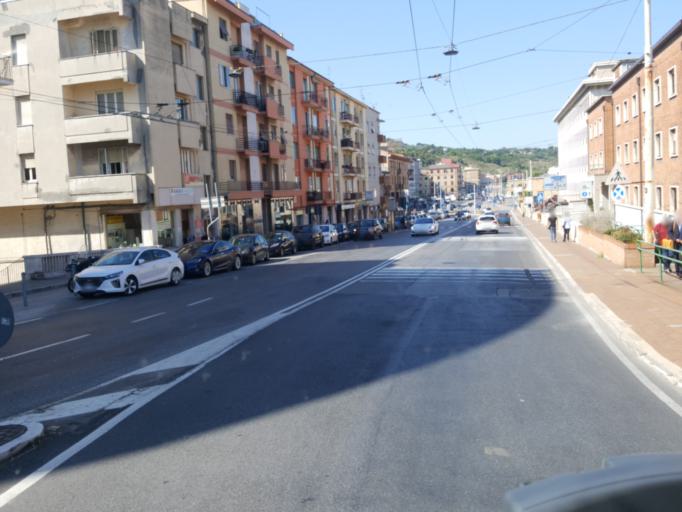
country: IT
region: The Marches
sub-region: Provincia di Ancona
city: Ancona
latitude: 43.6083
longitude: 13.5021
